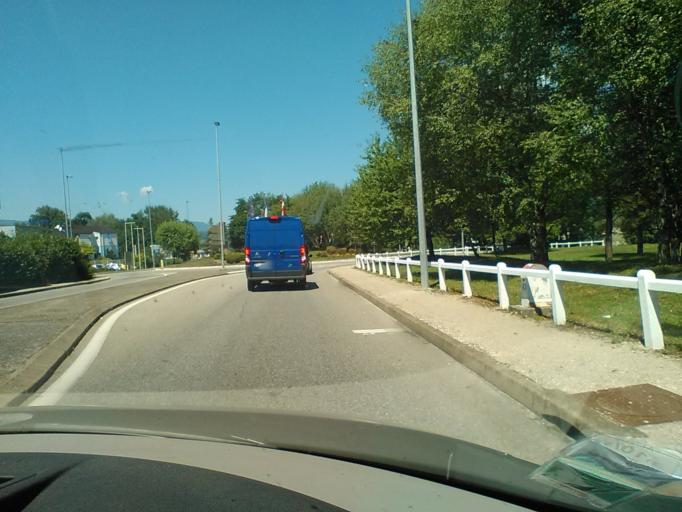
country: FR
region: Rhone-Alpes
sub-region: Departement de la Savoie
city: Challes-les-Eaux
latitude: 45.5551
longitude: 5.9783
